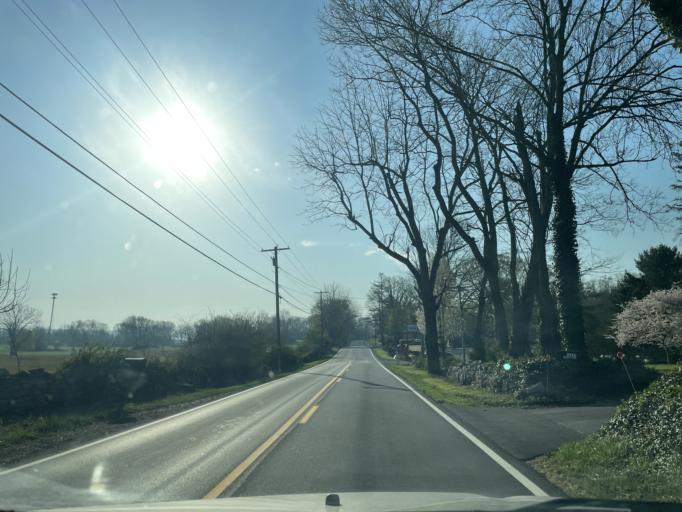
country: US
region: Maryland
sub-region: Washington County
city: Saint James
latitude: 39.5511
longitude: -77.7324
